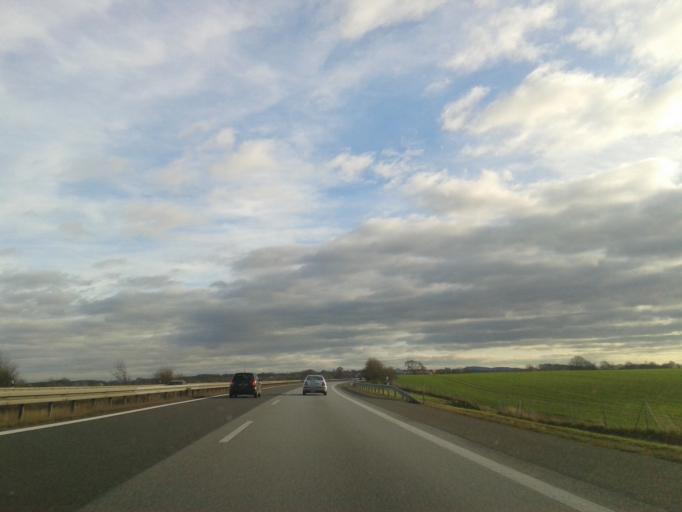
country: DE
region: Saxony
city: Goda
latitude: 51.2025
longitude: 14.3162
